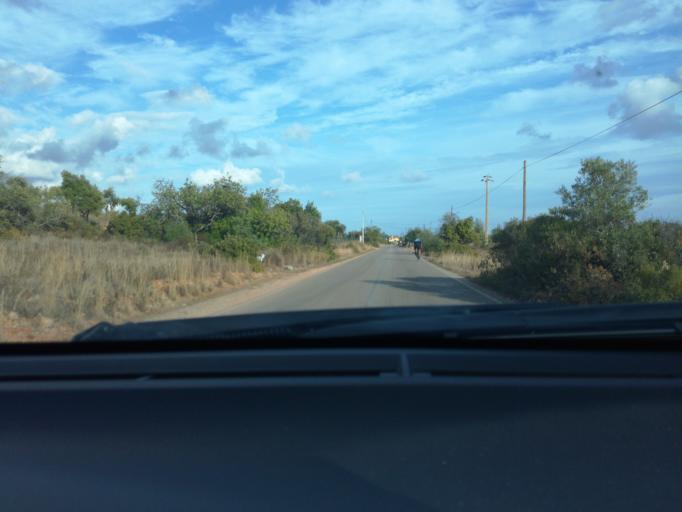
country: PT
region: Faro
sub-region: Olhao
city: Laranjeiro
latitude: 37.0781
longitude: -7.8251
